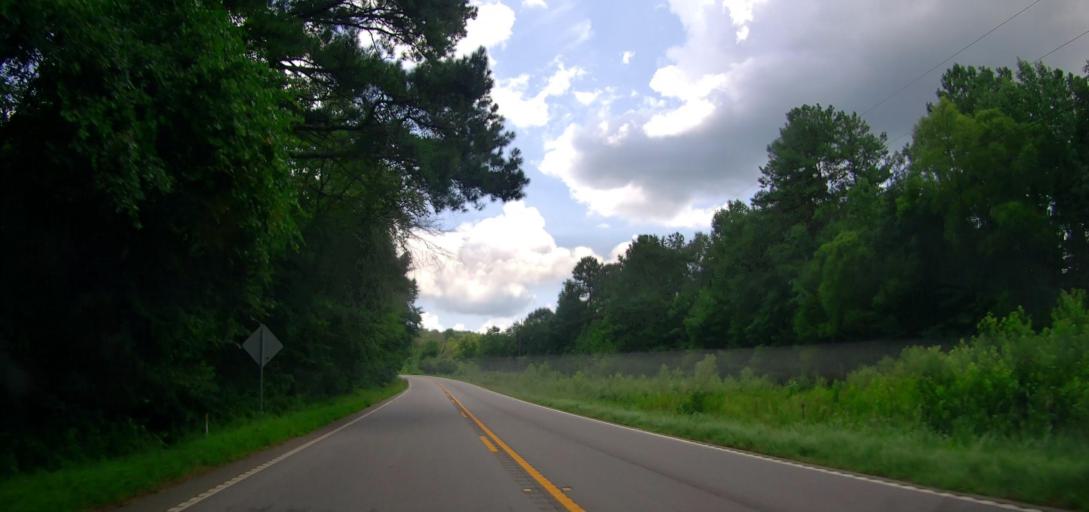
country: US
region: Georgia
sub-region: Meriwether County
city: Greenville
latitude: 33.0139
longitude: -84.6704
